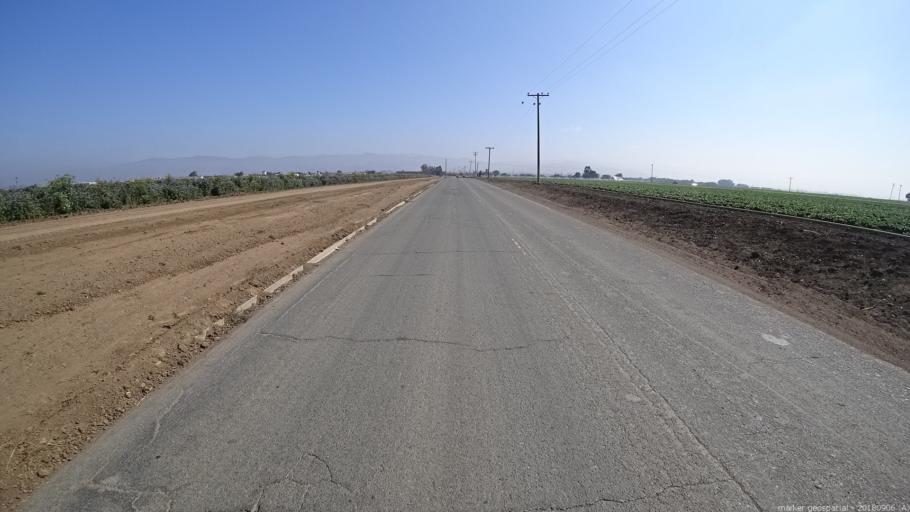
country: US
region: California
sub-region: Monterey County
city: Chualar
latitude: 36.5623
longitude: -121.5224
